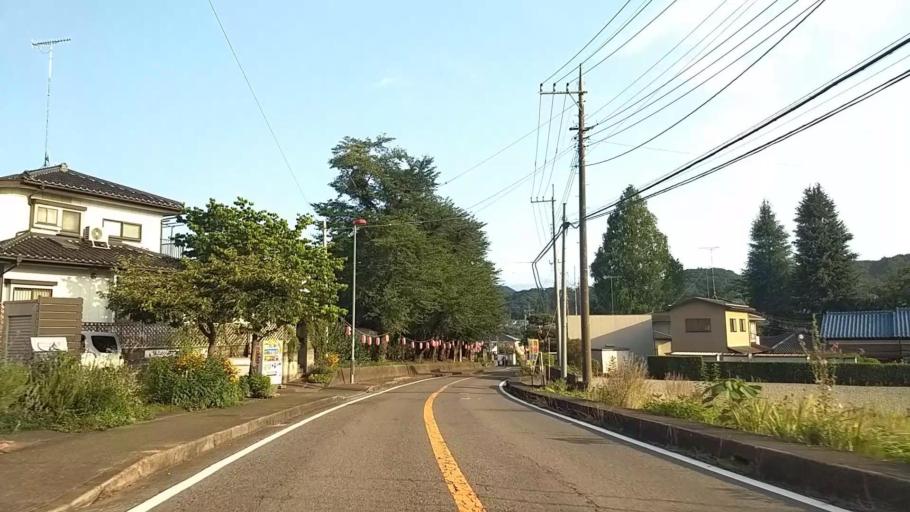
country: JP
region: Tokyo
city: Hachioji
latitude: 35.5931
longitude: 139.2627
